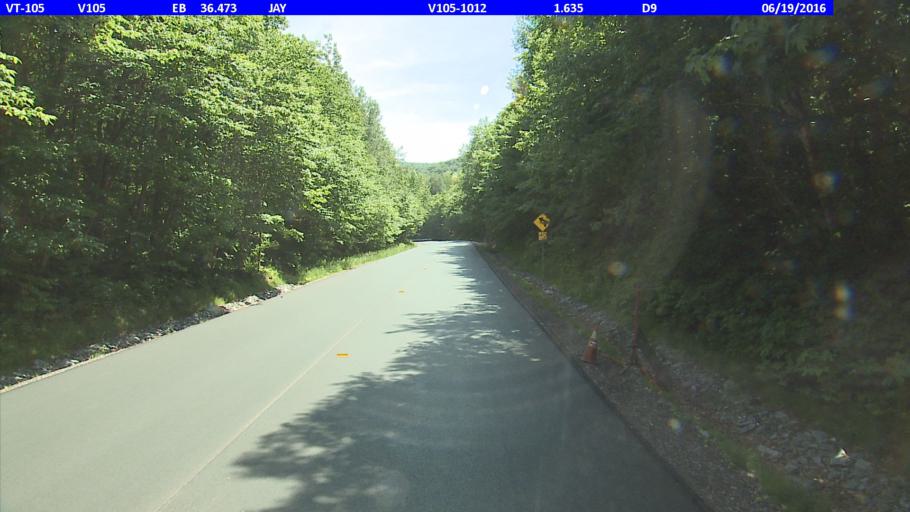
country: US
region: Vermont
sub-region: Franklin County
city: Richford
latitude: 44.9729
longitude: -72.5266
